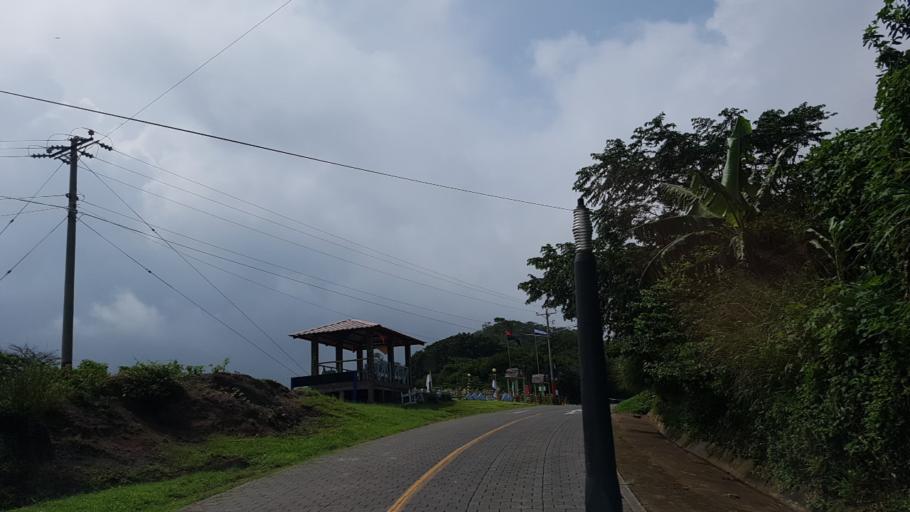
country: NI
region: Leon
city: Santa Rosa del Penon
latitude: 12.9388
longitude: -86.3396
